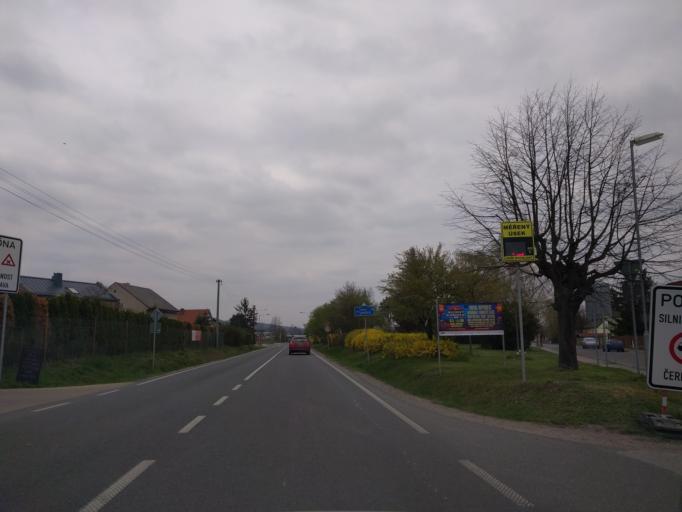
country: CZ
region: Central Bohemia
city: Revnice
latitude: 49.9199
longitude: 14.2495
